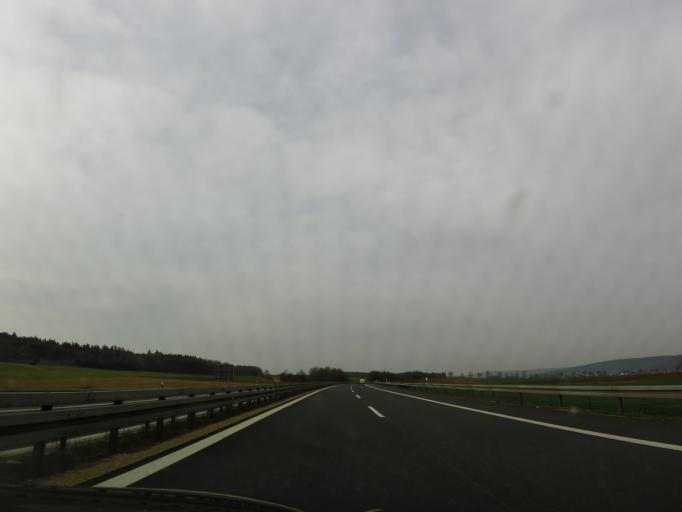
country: DE
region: Bavaria
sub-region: Upper Franconia
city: Bad Staffelstein
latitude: 50.0742
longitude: 10.9941
